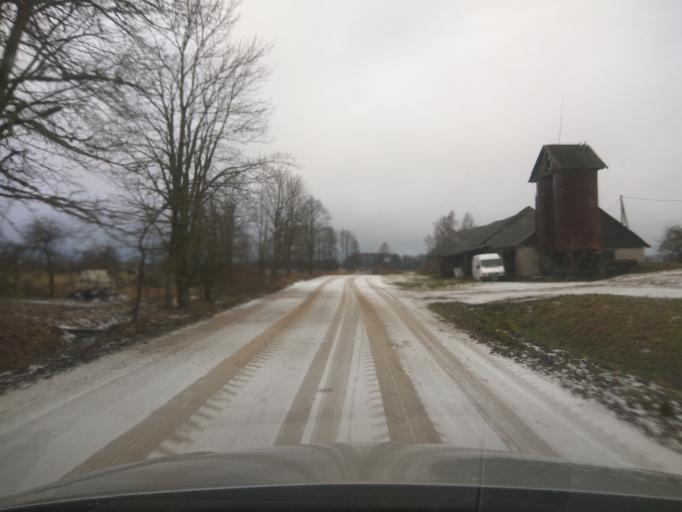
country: LV
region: Saldus Rajons
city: Saldus
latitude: 56.8095
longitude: 22.3139
